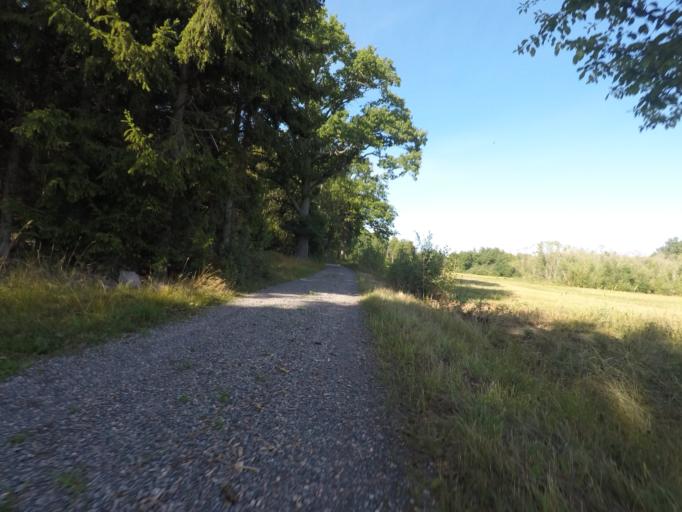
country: SE
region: Soedermanland
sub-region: Eskilstuna Kommun
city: Kvicksund
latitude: 59.4423
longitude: 16.2701
